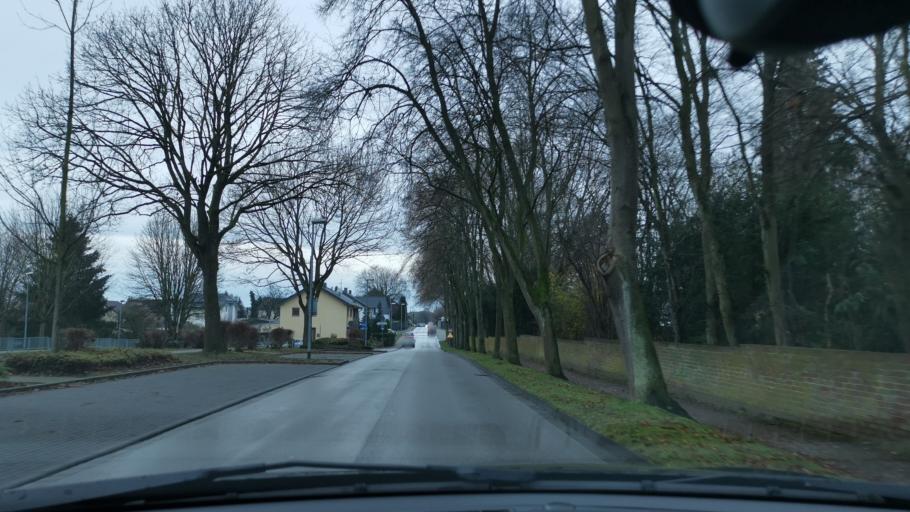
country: DE
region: North Rhine-Westphalia
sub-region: Regierungsbezirk Koln
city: Bedburg
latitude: 50.9869
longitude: 6.5638
